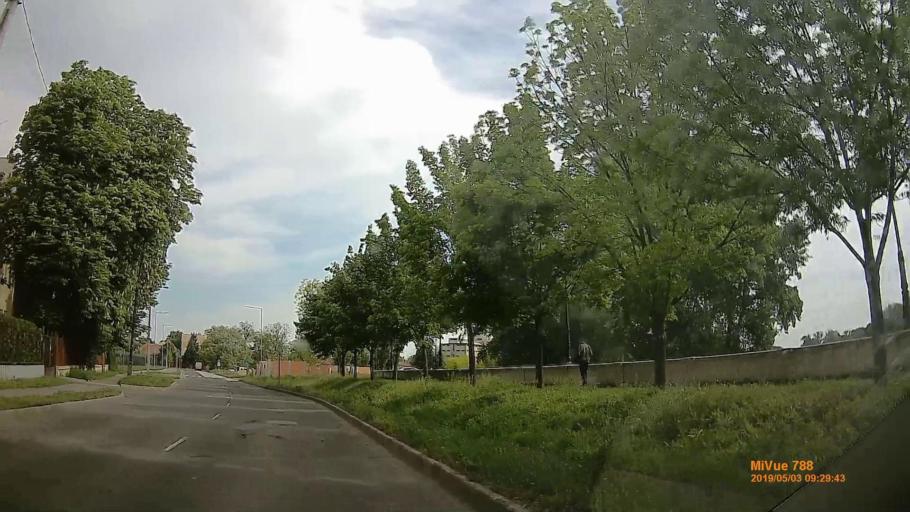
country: HU
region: Jasz-Nagykun-Szolnok
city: Szolnok
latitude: 47.1659
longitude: 20.1815
